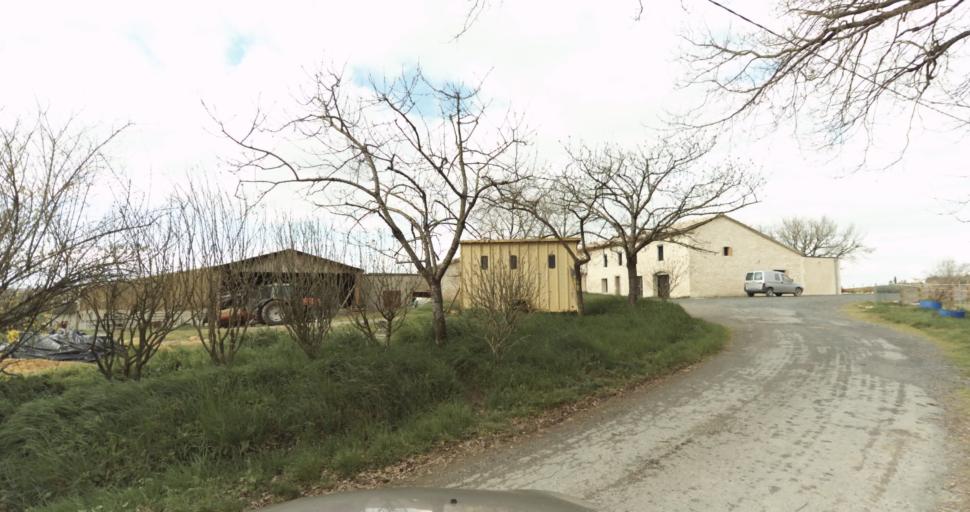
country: FR
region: Midi-Pyrenees
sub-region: Departement du Tarn
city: Frejairolles
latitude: 43.8597
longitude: 2.2176
